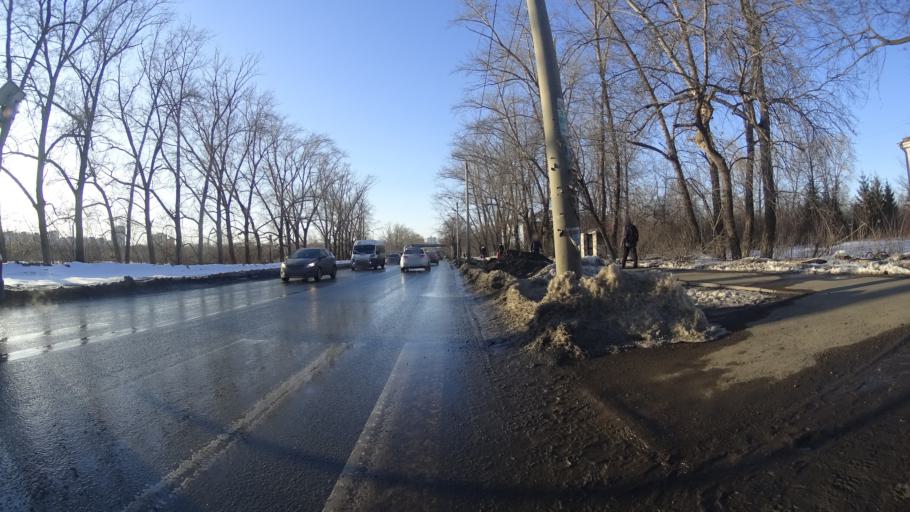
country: RU
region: Chelyabinsk
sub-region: Gorod Chelyabinsk
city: Chelyabinsk
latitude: 55.1310
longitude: 61.4639
